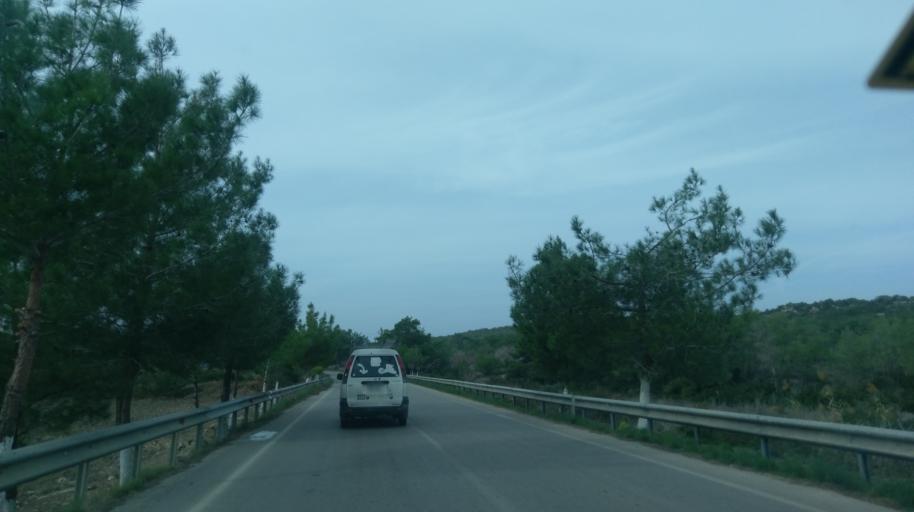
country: CY
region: Ammochostos
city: Leonarisso
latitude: 35.4463
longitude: 34.1349
